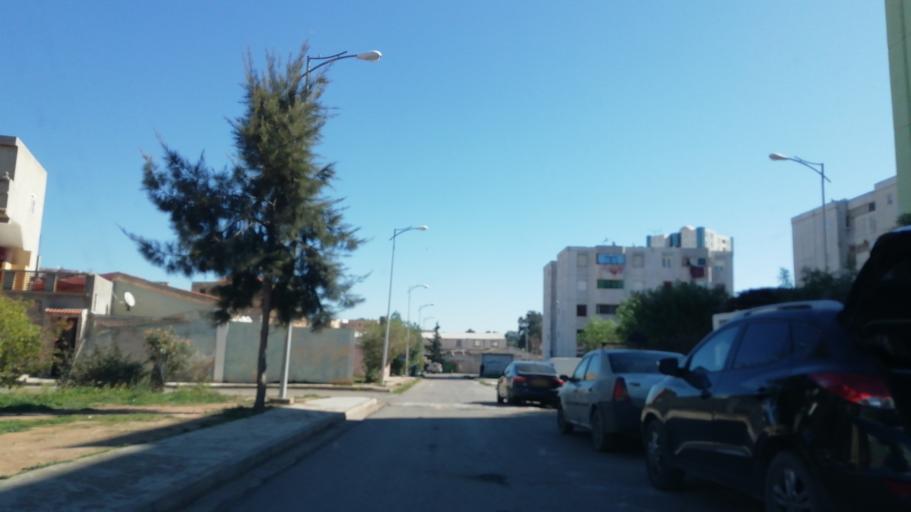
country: DZ
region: Oran
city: Oran
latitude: 35.6886
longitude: -0.6107
